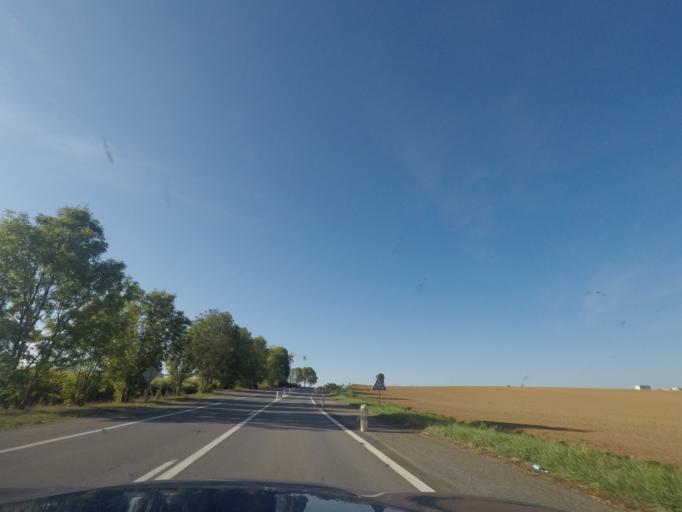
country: LU
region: Luxembourg
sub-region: Canton d'Esch-sur-Alzette
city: Frisange
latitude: 49.4649
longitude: 6.1830
